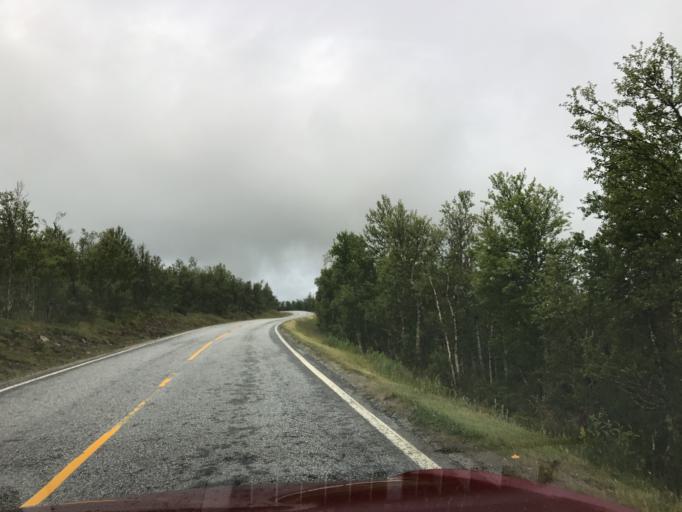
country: NO
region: Buskerud
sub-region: Hol
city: Hol
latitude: 60.4380
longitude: 8.3991
